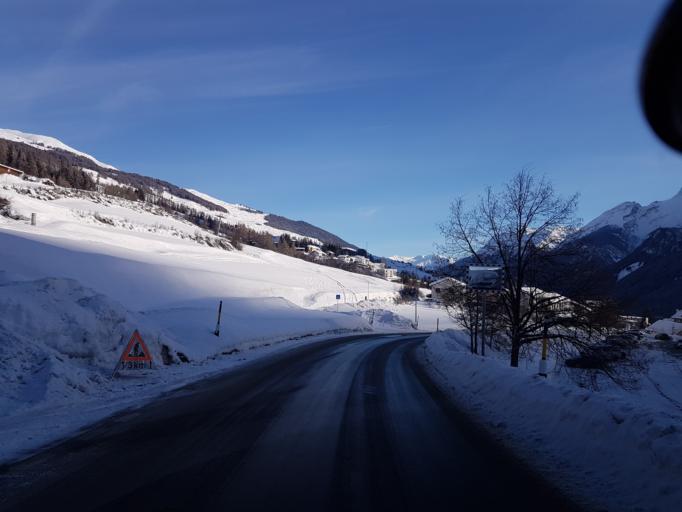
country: CH
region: Grisons
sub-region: Inn District
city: Scuol
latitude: 46.7945
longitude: 10.2849
